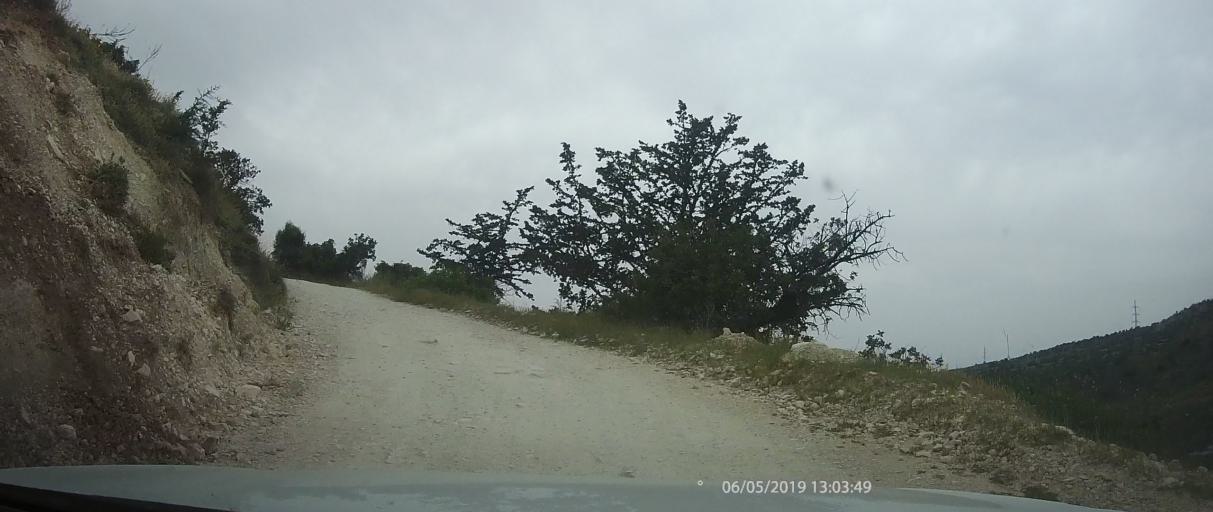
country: CY
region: Pafos
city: Tala
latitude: 34.8670
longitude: 32.4336
